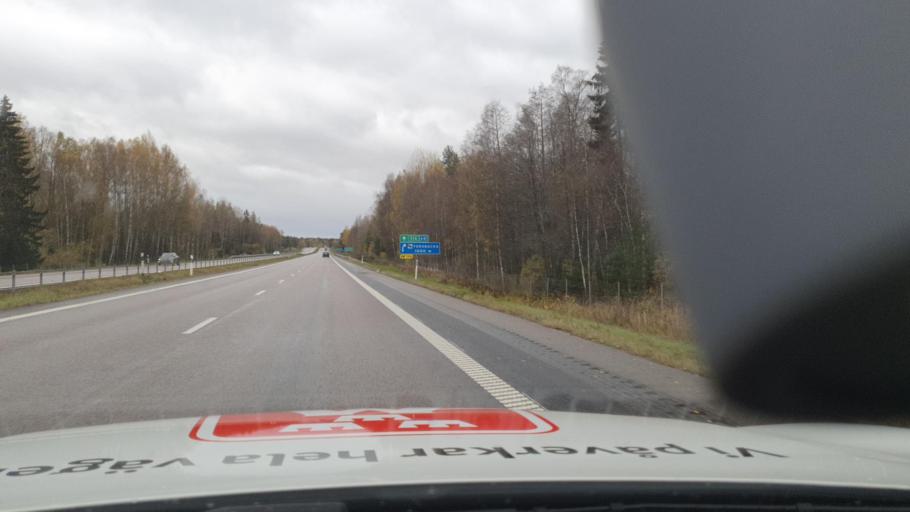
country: SE
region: Gaevleborg
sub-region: Gavle Kommun
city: Valbo
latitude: 60.6276
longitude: 16.9177
